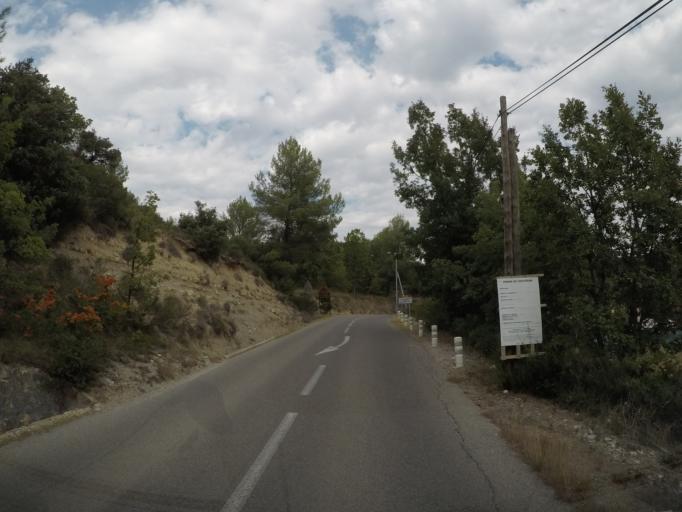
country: FR
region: Provence-Alpes-Cote d'Azur
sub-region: Departement des Alpes-de-Haute-Provence
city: Greoux-les-Bains
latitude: 43.7639
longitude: 5.8895
